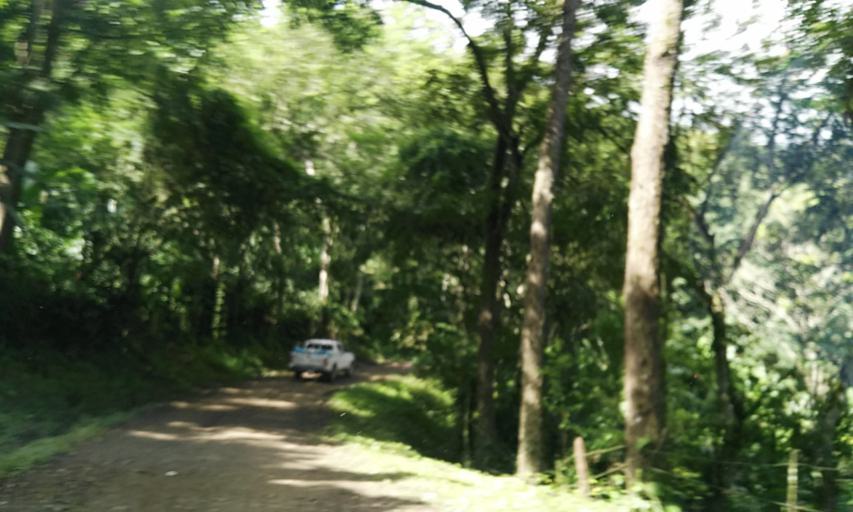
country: NI
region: Matagalpa
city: San Ramon
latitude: 12.9881
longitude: -85.8497
